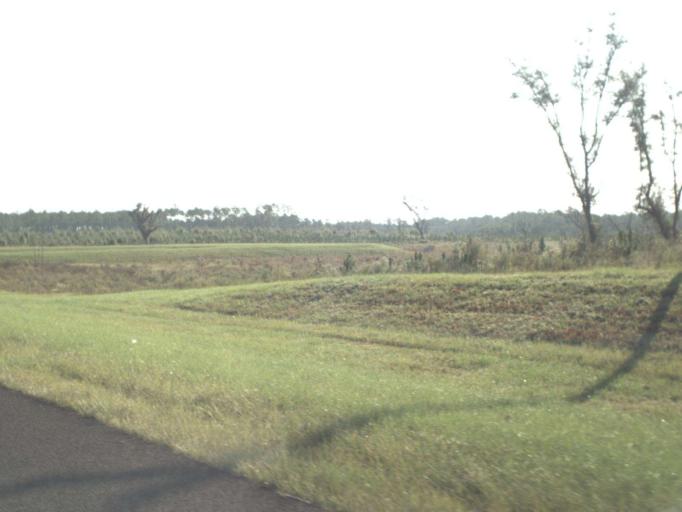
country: US
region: Florida
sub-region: Bay County
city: Laguna Beach
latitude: 30.4715
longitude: -85.8504
